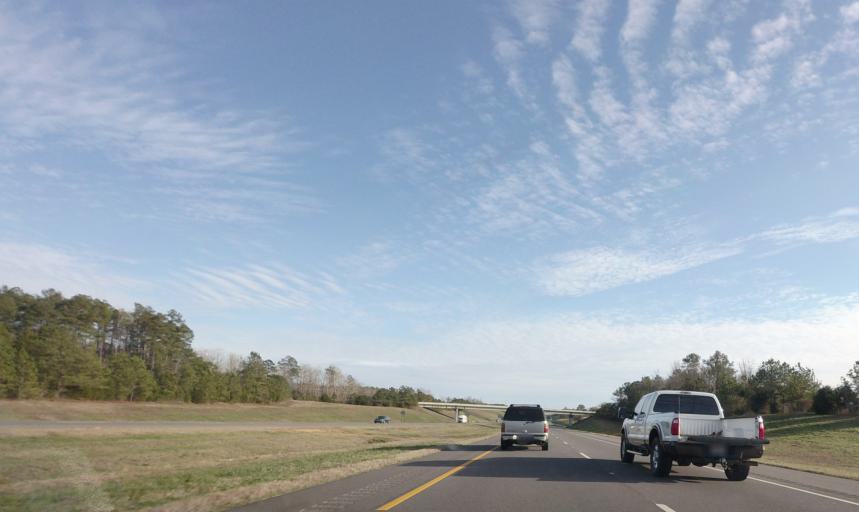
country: US
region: Alabama
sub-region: Walker County
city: Jasper
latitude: 33.8417
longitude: -87.3334
